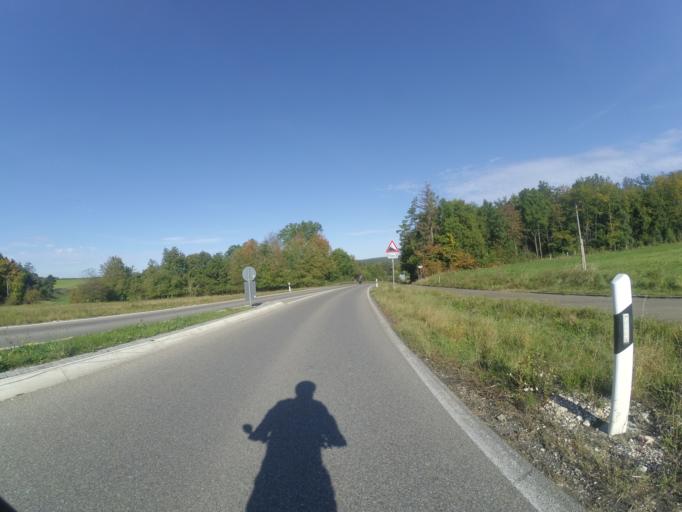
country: DE
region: Baden-Wuerttemberg
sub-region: Tuebingen Region
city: Breitingen
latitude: 48.5057
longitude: 9.9882
